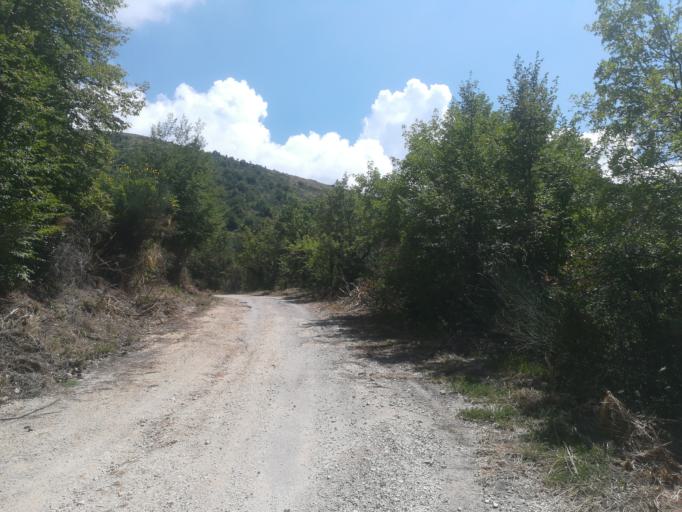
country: IT
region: Umbria
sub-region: Provincia di Perugia
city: Scheggino
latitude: 42.6753
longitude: 12.8535
